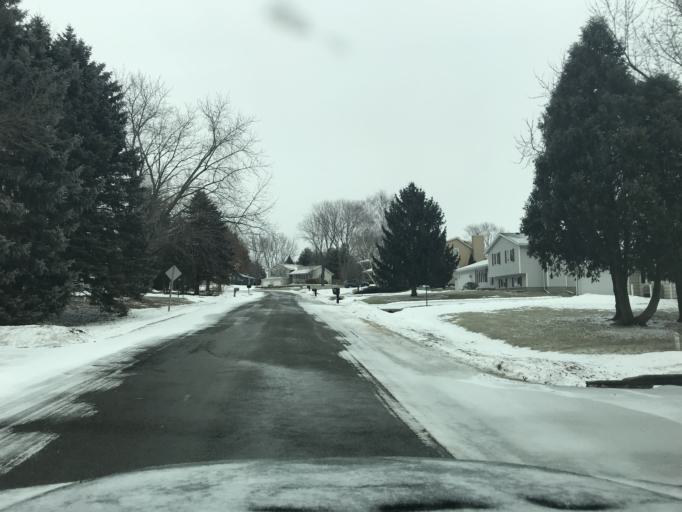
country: US
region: Wisconsin
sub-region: Dane County
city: Cottage Grove
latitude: 43.0938
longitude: -89.2330
